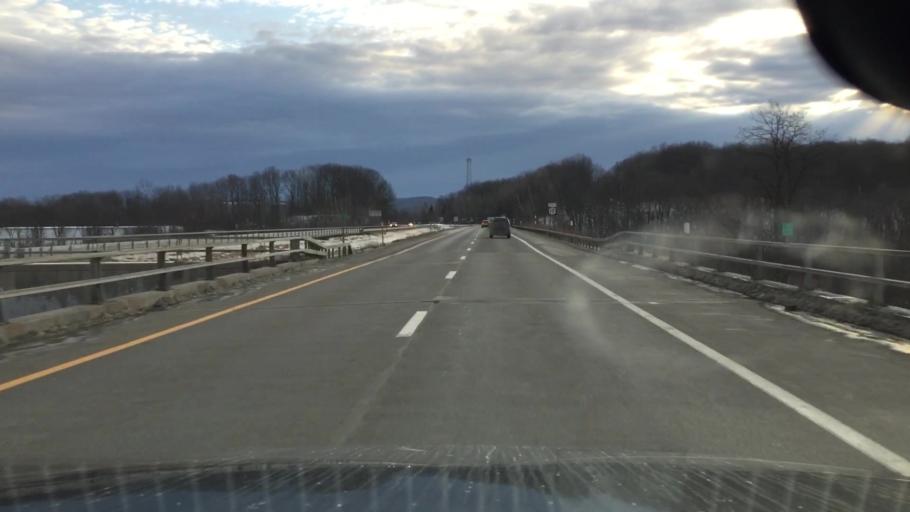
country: US
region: New York
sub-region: Tioga County
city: Waverly
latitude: 42.0000
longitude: -76.5212
